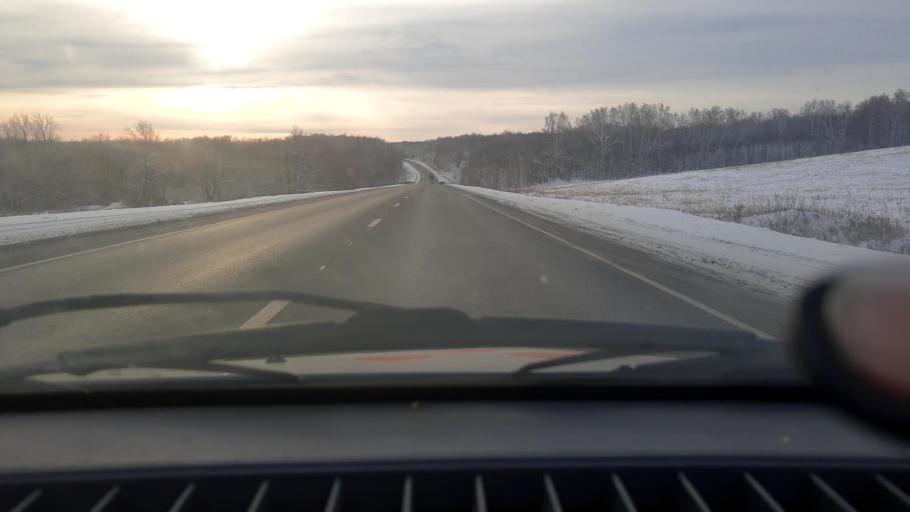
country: RU
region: Bashkortostan
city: Avdon
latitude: 54.8294
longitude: 55.7261
